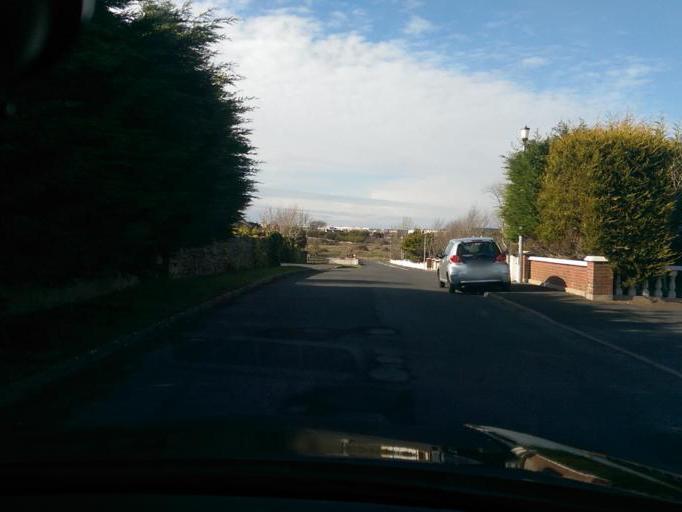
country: IE
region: Connaught
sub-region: County Galway
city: Oranmore
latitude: 53.2711
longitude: -8.9217
